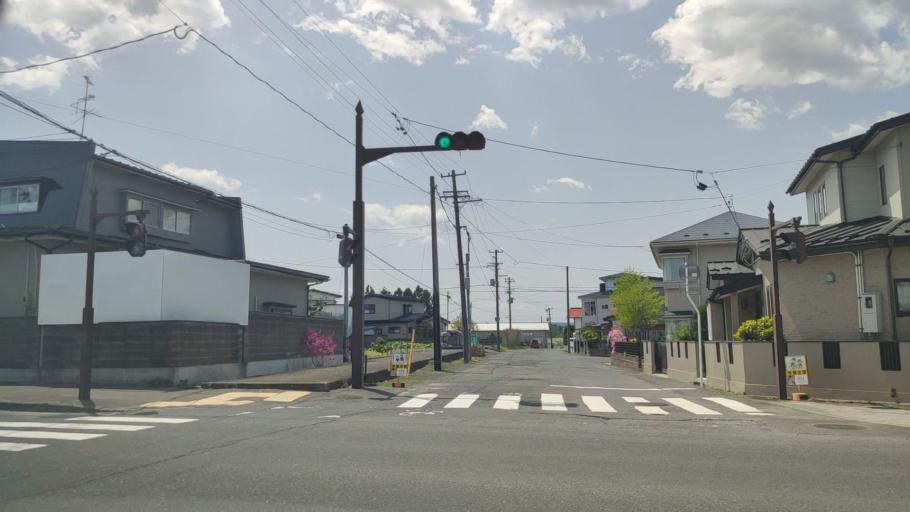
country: JP
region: Aomori
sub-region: Hachinohe Shi
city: Uchimaru
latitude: 40.5072
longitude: 141.4355
